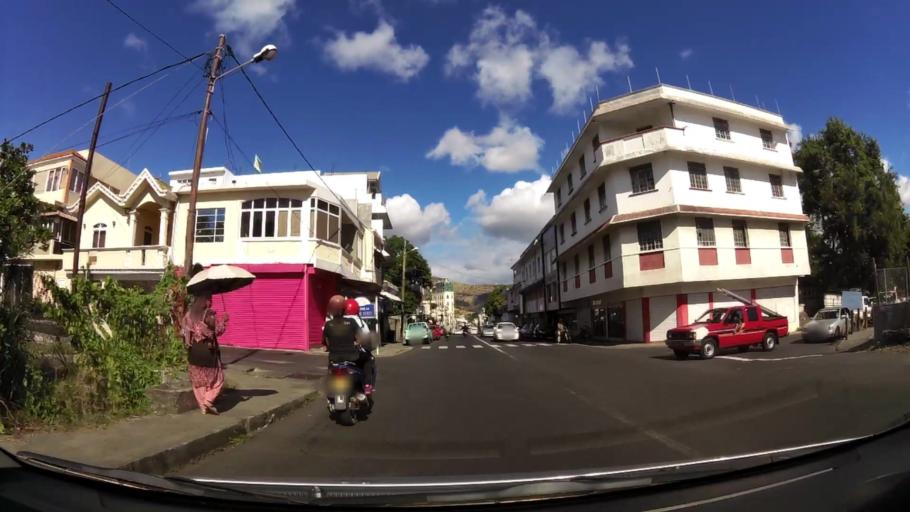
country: MU
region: Pamplemousses
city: Le Hochet
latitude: -20.1542
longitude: 57.5192
